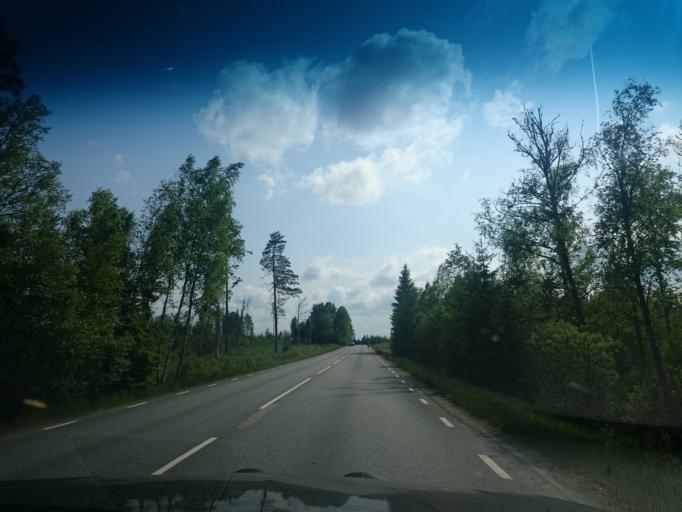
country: SE
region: Joenkoeping
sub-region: Vetlanda Kommun
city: Landsbro
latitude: 57.3990
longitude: 14.9882
